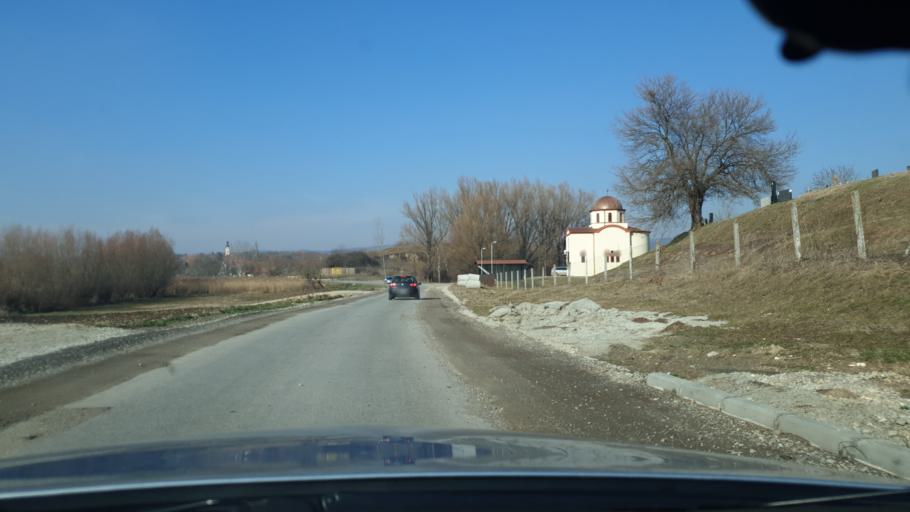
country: RS
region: Autonomna Pokrajina Vojvodina
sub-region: Sremski Okrug
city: Irig
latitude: 45.0821
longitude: 19.8403
